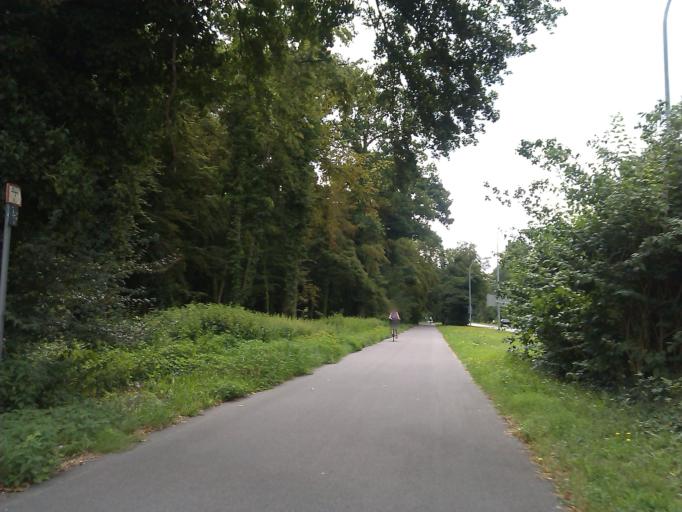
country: DE
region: Rheinland-Pfalz
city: Schifferstadt
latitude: 49.3704
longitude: 8.3854
